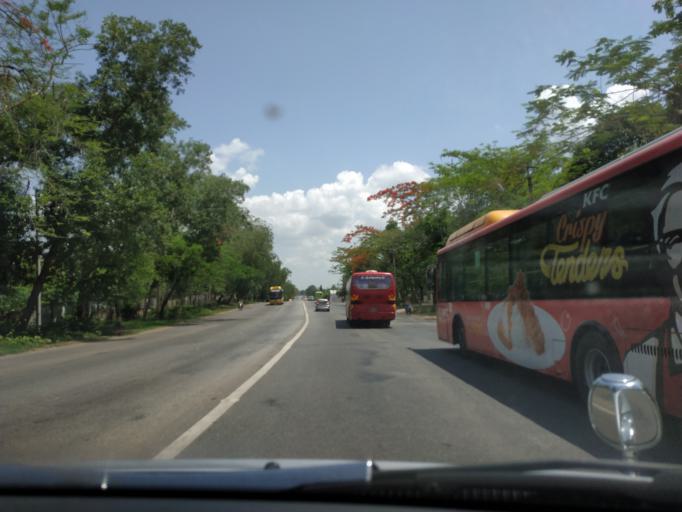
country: MM
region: Yangon
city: Yangon
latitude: 16.9925
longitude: 96.1312
